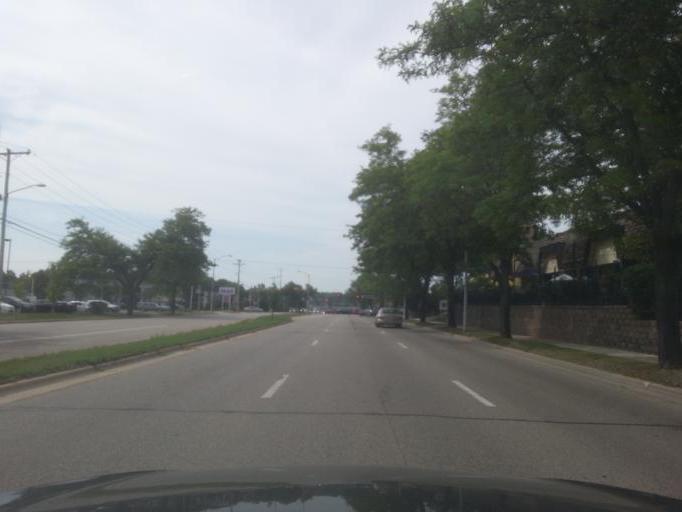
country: US
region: Wisconsin
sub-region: Dane County
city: Shorewood Hills
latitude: 43.0515
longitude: -89.4736
